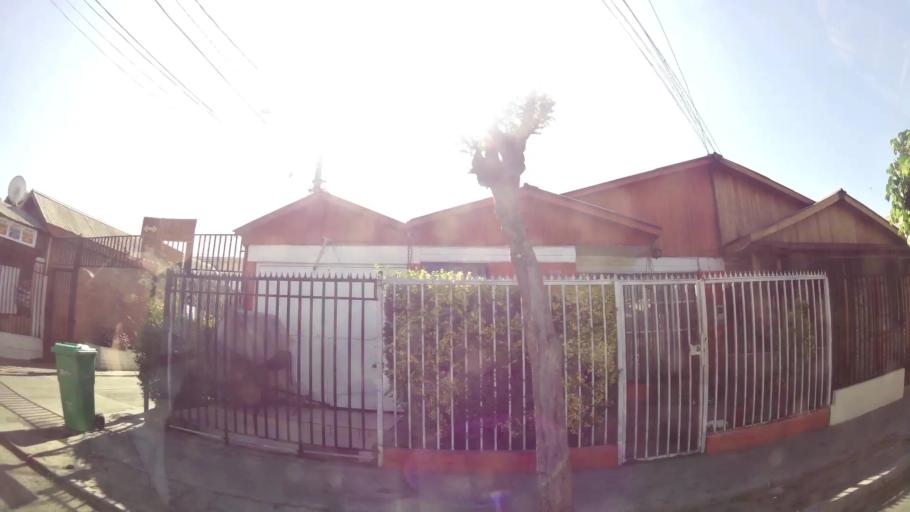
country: CL
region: Santiago Metropolitan
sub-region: Provincia de Maipo
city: San Bernardo
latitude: -33.5713
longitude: -70.7052
